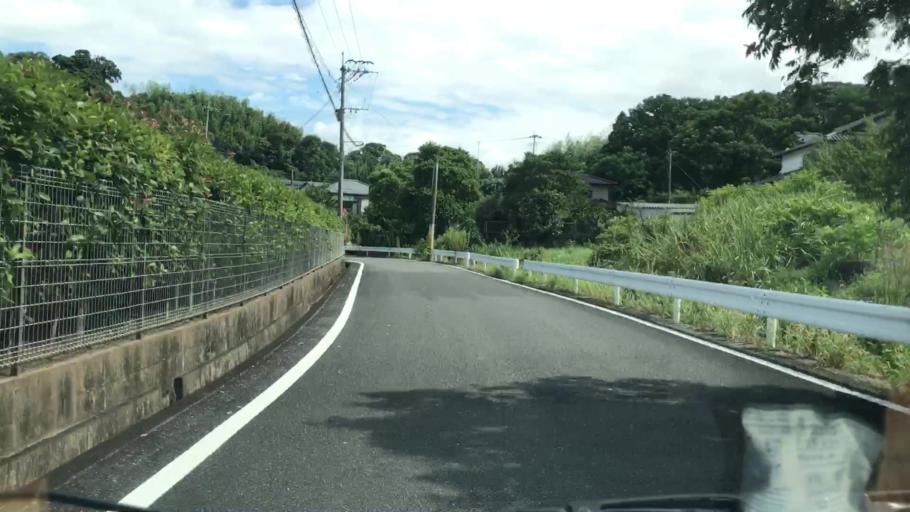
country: JP
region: Saga Prefecture
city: Saga-shi
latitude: 33.2296
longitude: 130.1782
